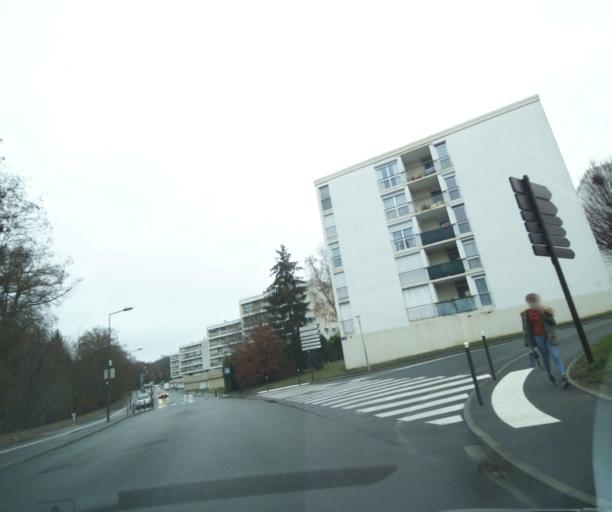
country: FR
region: Ile-de-France
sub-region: Departement de Seine-et-Marne
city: Avon
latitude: 48.4135
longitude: 2.7364
